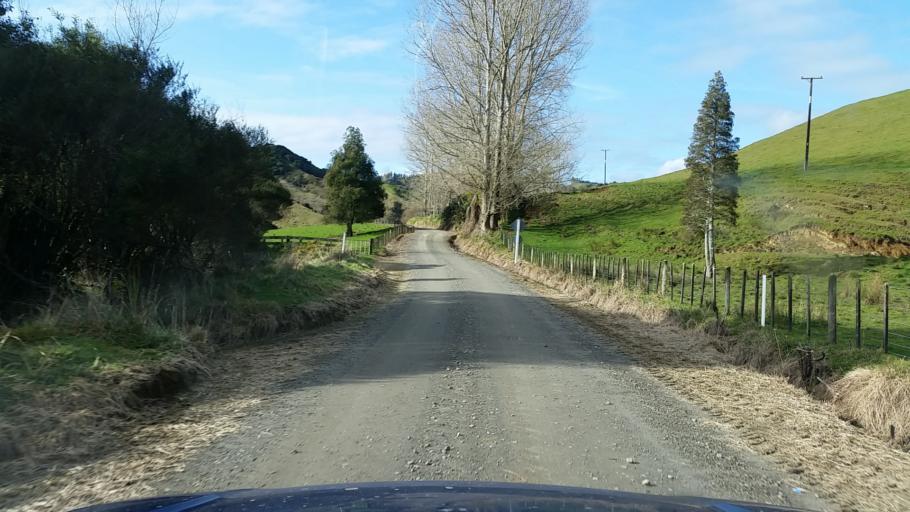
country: NZ
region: Taranaki
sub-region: South Taranaki District
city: Eltham
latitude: -39.2610
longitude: 174.5830
